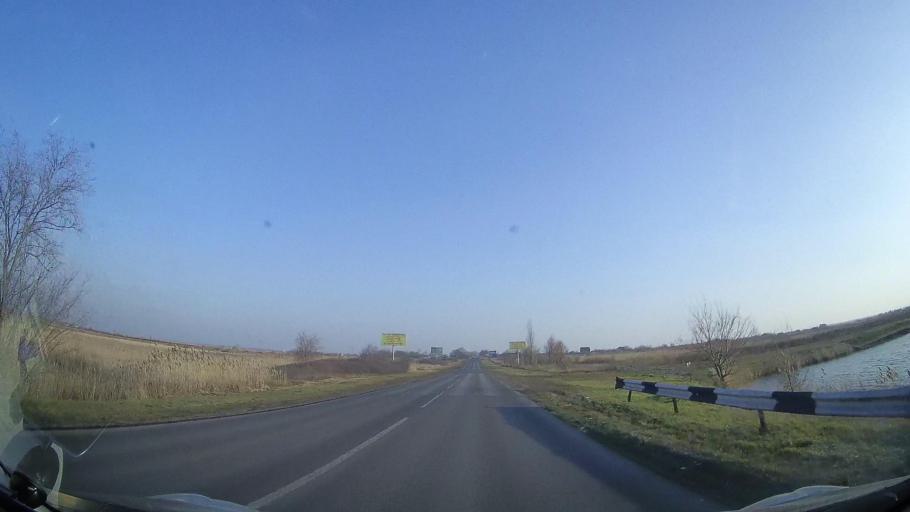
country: RU
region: Rostov
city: Ol'ginskaya
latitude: 47.2046
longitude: 39.9274
